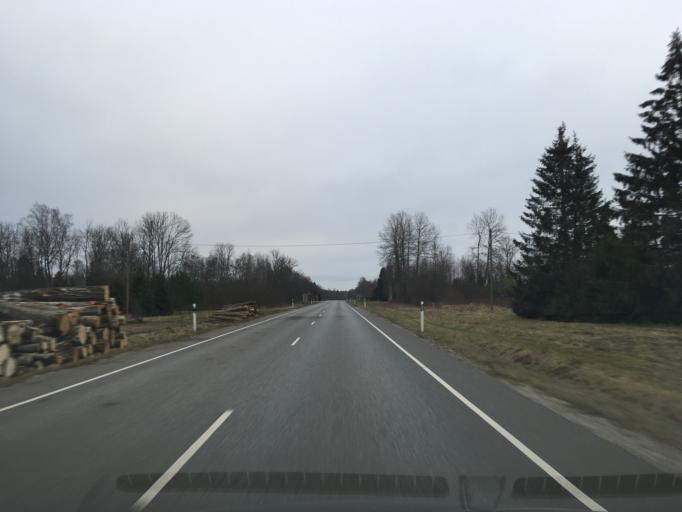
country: EE
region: Laeaene-Virumaa
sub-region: Kadrina vald
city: Kadrina
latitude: 59.4510
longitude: 26.0418
